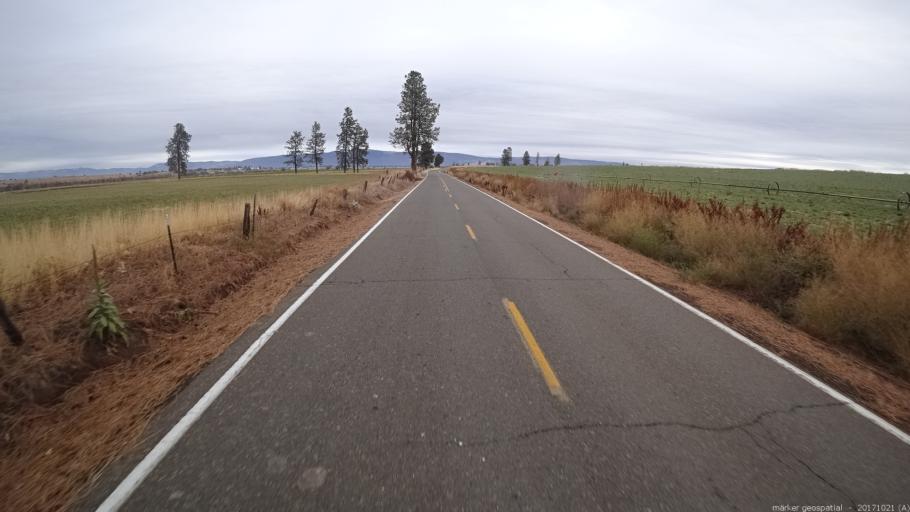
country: US
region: California
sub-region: Shasta County
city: Burney
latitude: 41.0228
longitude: -121.4073
